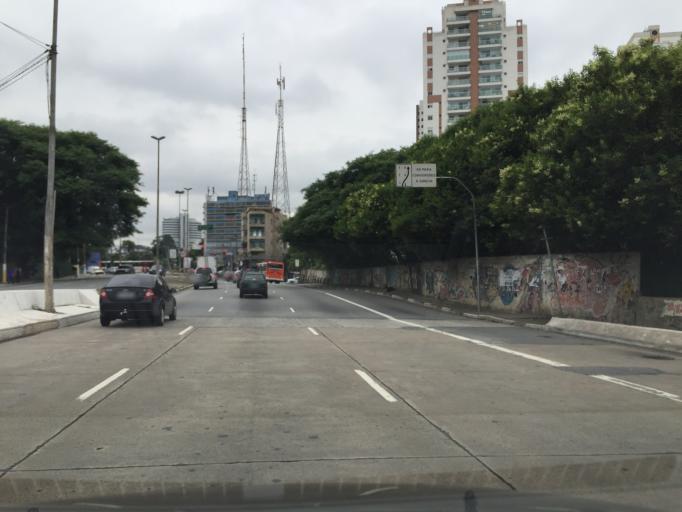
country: BR
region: Sao Paulo
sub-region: Sao Paulo
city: Sao Paulo
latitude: -23.5513
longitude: -46.6773
